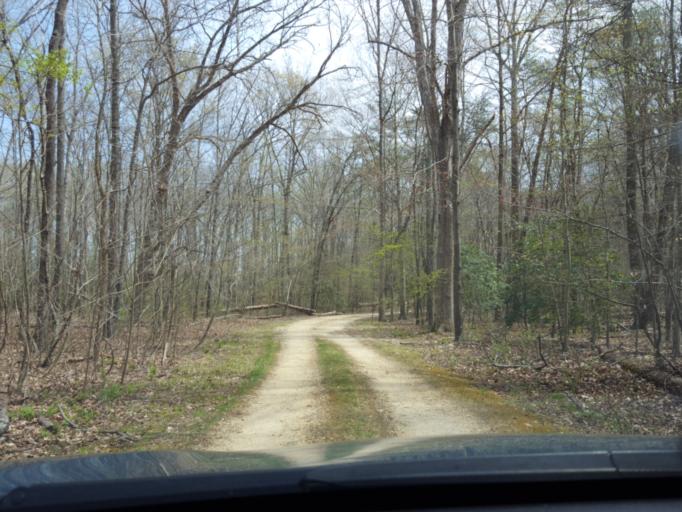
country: US
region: Maryland
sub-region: Calvert County
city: Dunkirk
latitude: 38.7430
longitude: -76.7070
